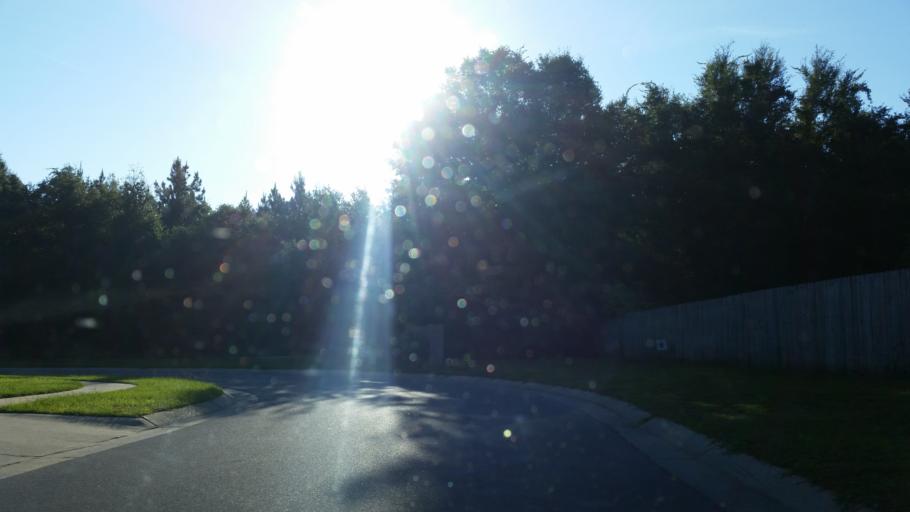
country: US
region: Florida
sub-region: Escambia County
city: Bellview
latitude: 30.4982
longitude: -87.3571
